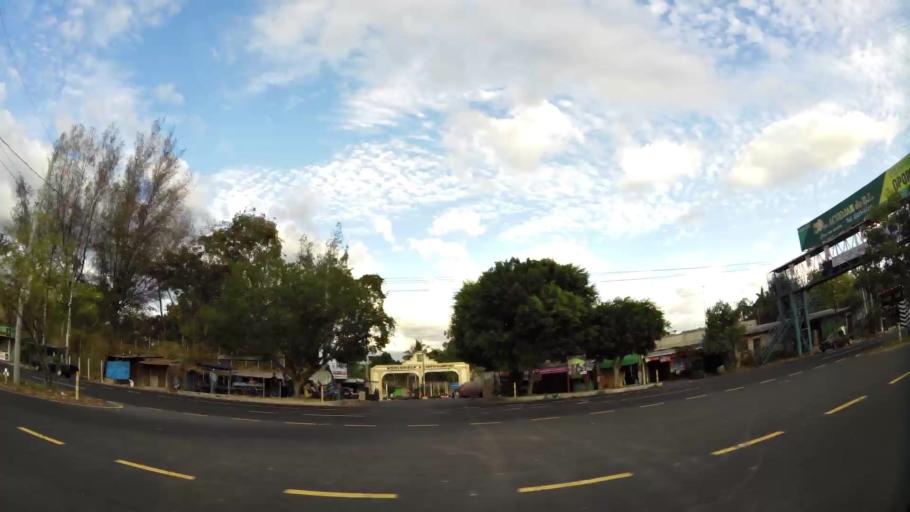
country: SV
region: San Vicente
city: San Sebastian
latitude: 13.7180
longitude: -88.8584
